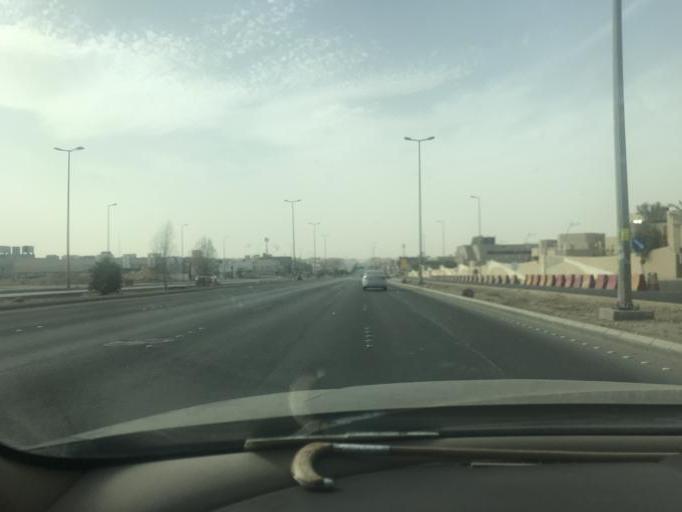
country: SA
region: Ar Riyad
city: Riyadh
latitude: 24.8238
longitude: 46.6850
